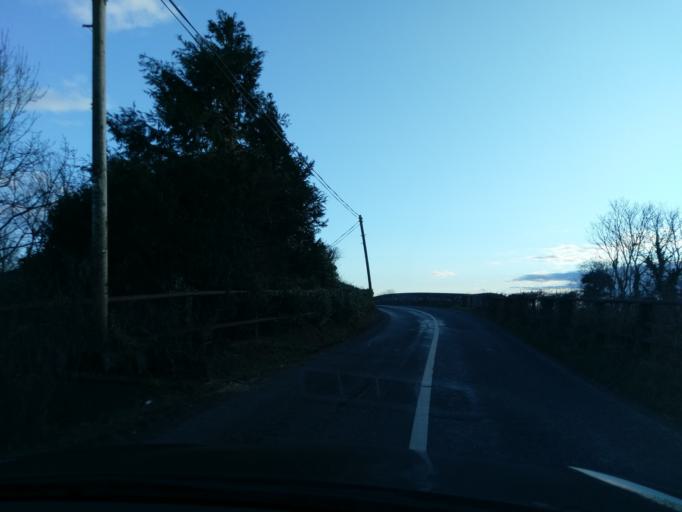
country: IE
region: Connaught
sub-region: County Galway
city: Loughrea
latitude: 53.3217
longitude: -8.6086
